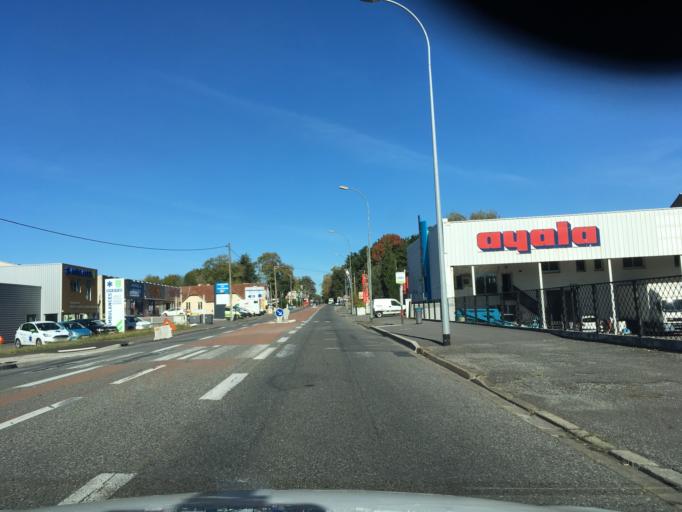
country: FR
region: Aquitaine
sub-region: Departement des Pyrenees-Atlantiques
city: Lons
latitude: 43.3324
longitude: -0.3797
